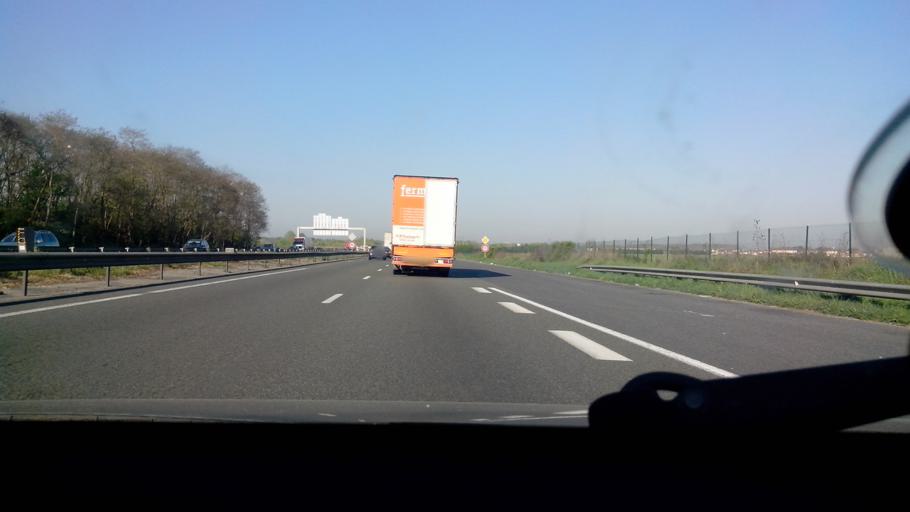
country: FR
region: Ile-de-France
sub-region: Departement de Seine-et-Marne
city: Lieusaint
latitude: 48.6321
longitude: 2.5269
